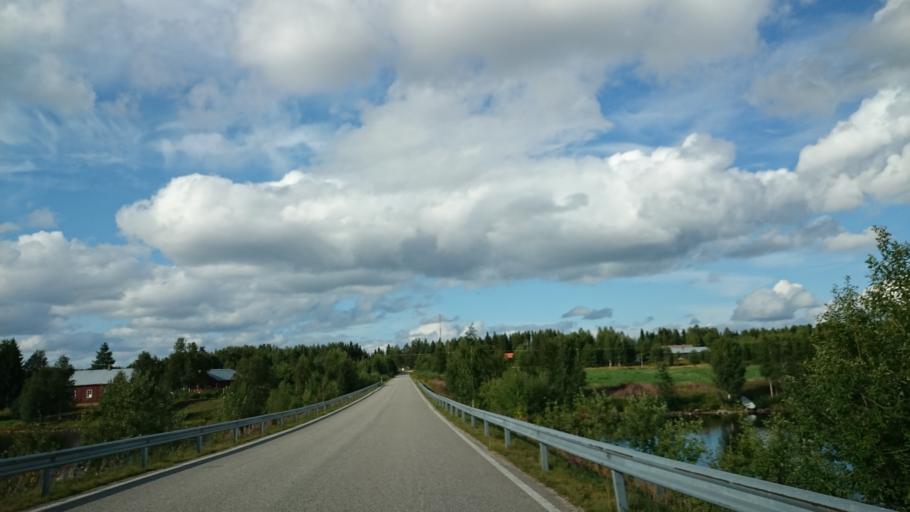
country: FI
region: Kainuu
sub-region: Kehys-Kainuu
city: Suomussalmi
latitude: 64.7430
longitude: 29.4396
